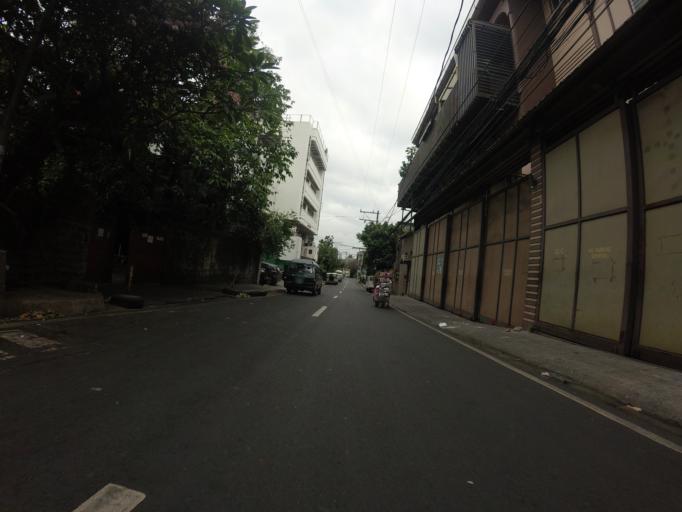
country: PH
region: Metro Manila
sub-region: San Juan
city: San Juan
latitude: 14.6070
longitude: 121.0313
